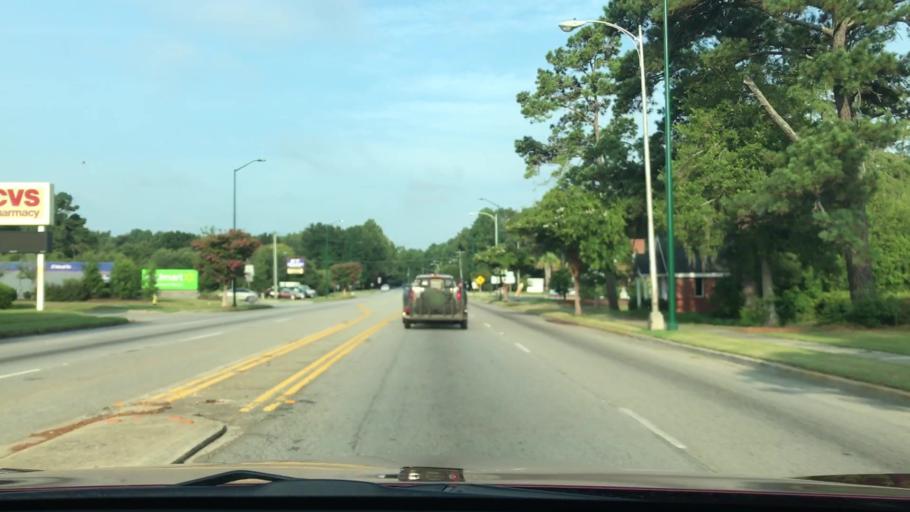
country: US
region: South Carolina
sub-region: Orangeburg County
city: Orangeburg
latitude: 33.4837
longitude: -80.8704
